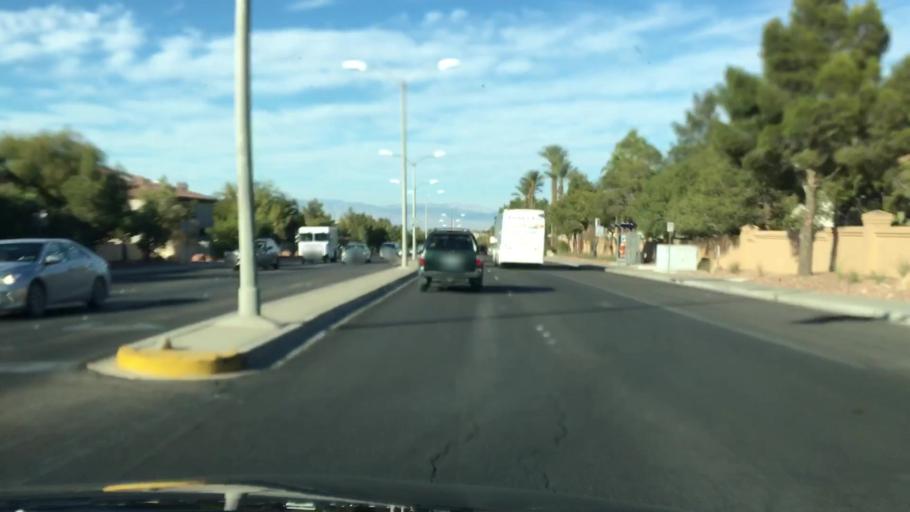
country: US
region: Nevada
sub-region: Clark County
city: Whitney
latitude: 36.0280
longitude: -115.1004
